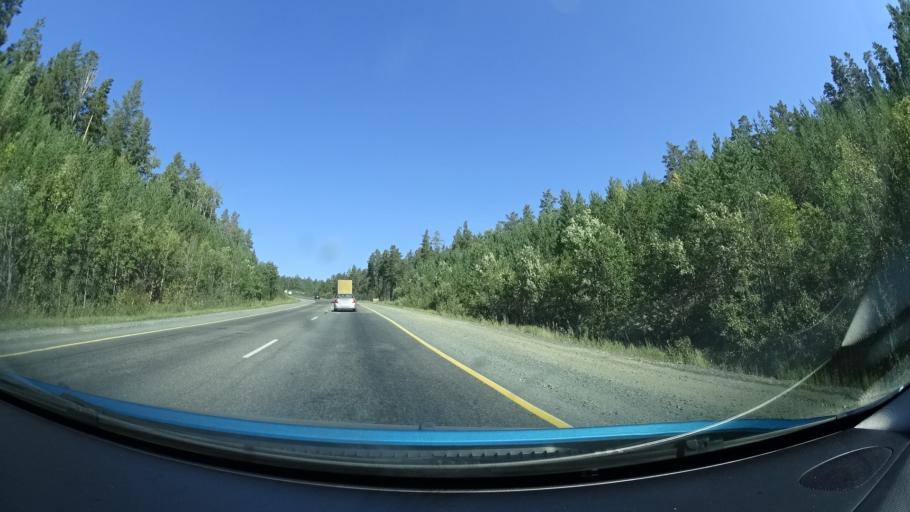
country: RU
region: Bashkortostan
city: Abzakovo
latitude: 53.8852
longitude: 58.5284
